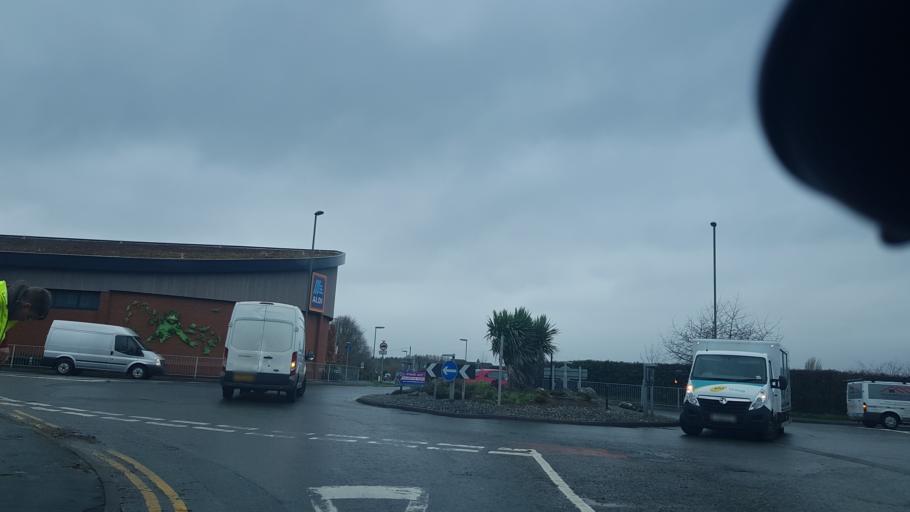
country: GB
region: England
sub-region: Surrey
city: Send
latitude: 51.2587
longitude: -0.5447
